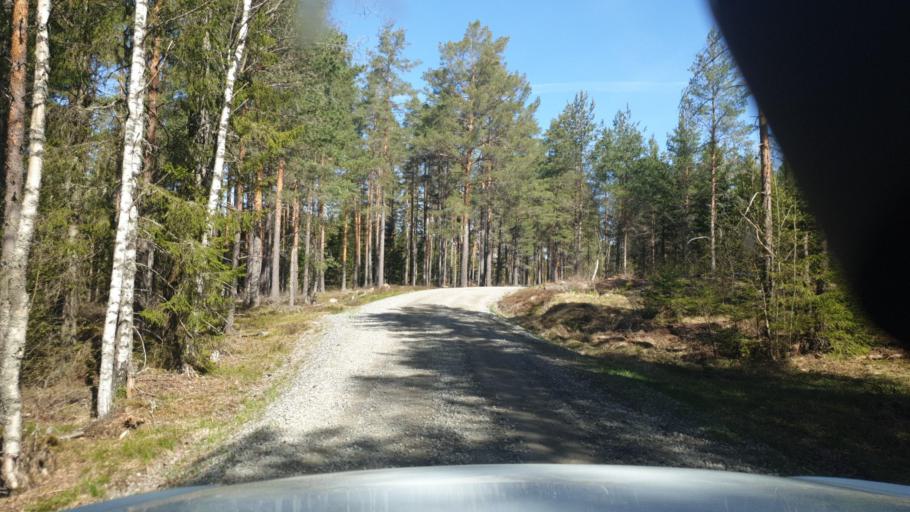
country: SE
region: Vaermland
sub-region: Karlstads Kommun
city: Edsvalla
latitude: 59.4594
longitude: 13.1001
